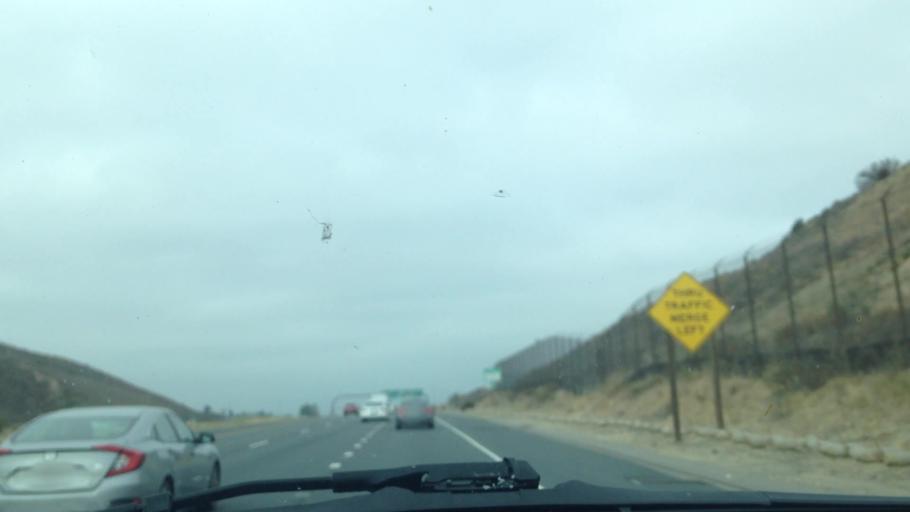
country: US
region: California
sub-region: Orange County
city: North Tustin
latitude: 33.7902
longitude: -117.7398
